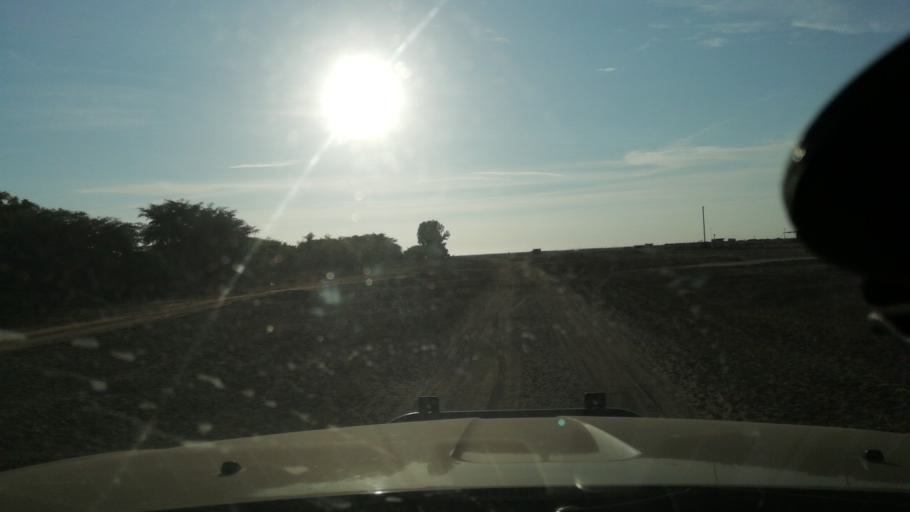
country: PE
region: Ica
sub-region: Provincia de Chincha
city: San Pedro
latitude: -13.3310
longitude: -76.1822
